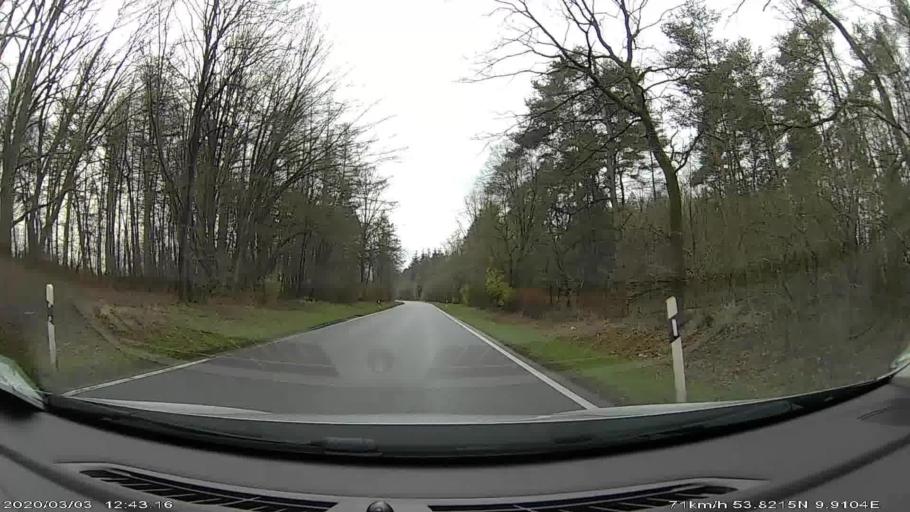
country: DE
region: Schleswig-Holstein
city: Alveslohe
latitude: 53.8203
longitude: 9.9080
